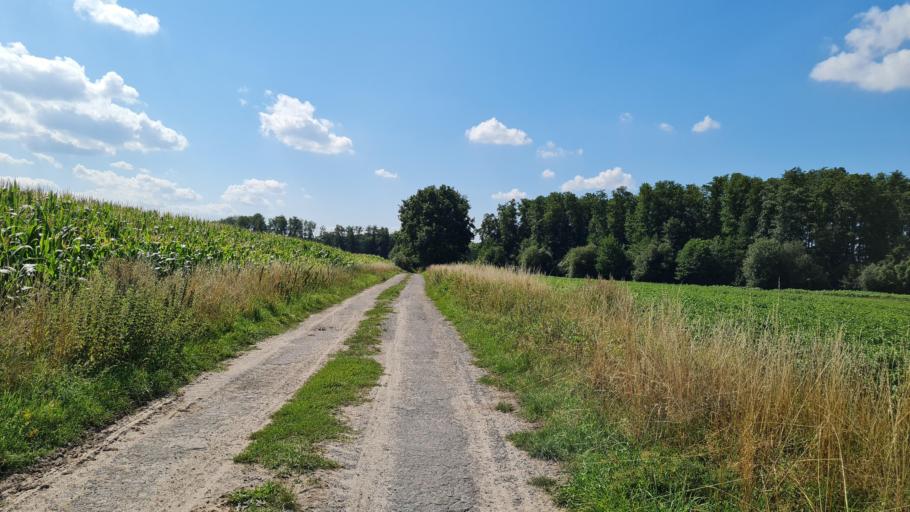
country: DE
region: Lower Saxony
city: Boitze
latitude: 53.1678
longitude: 10.7618
